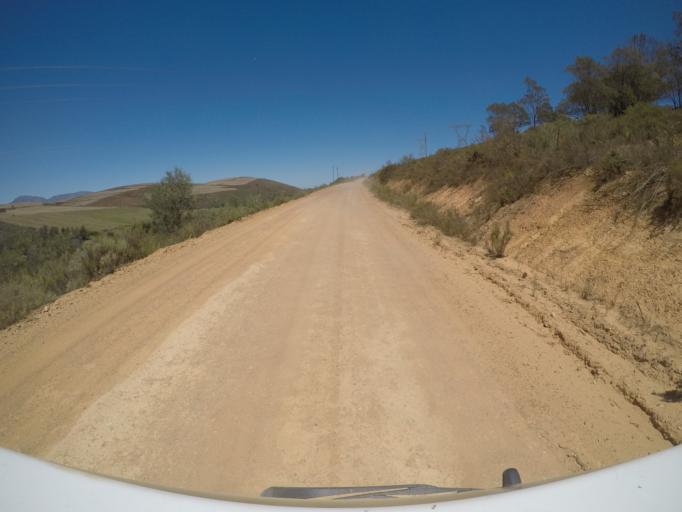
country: ZA
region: Western Cape
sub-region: Overberg District Municipality
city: Caledon
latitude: -34.2020
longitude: 19.2195
